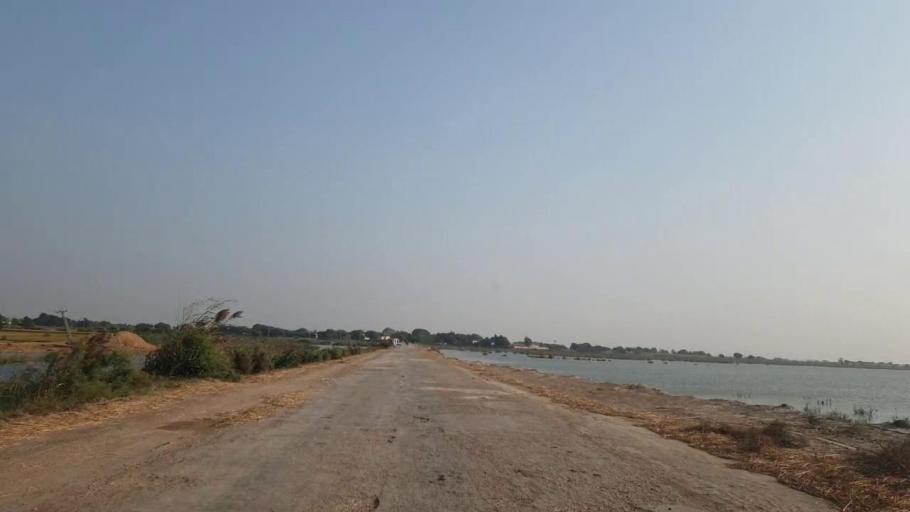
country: PK
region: Sindh
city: Bulri
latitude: 24.9907
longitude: 68.3875
